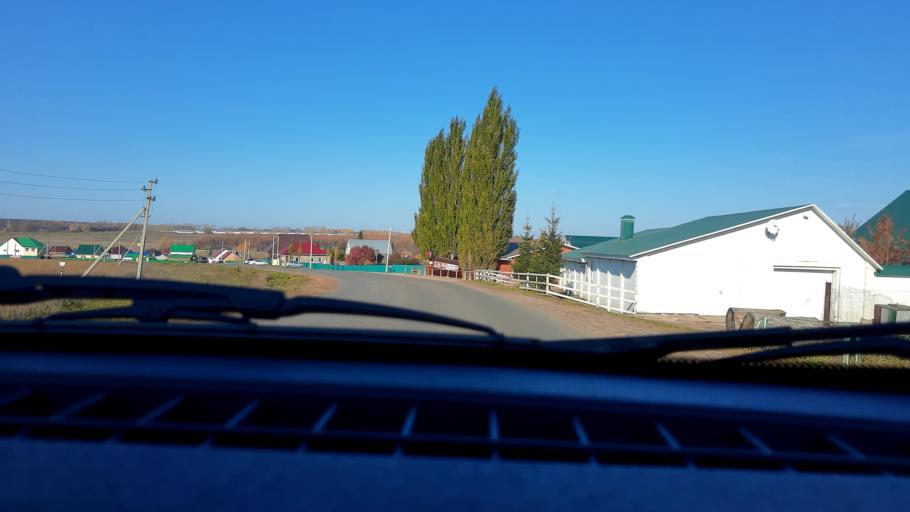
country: RU
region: Bashkortostan
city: Mikhaylovka
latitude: 54.8137
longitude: 55.7890
